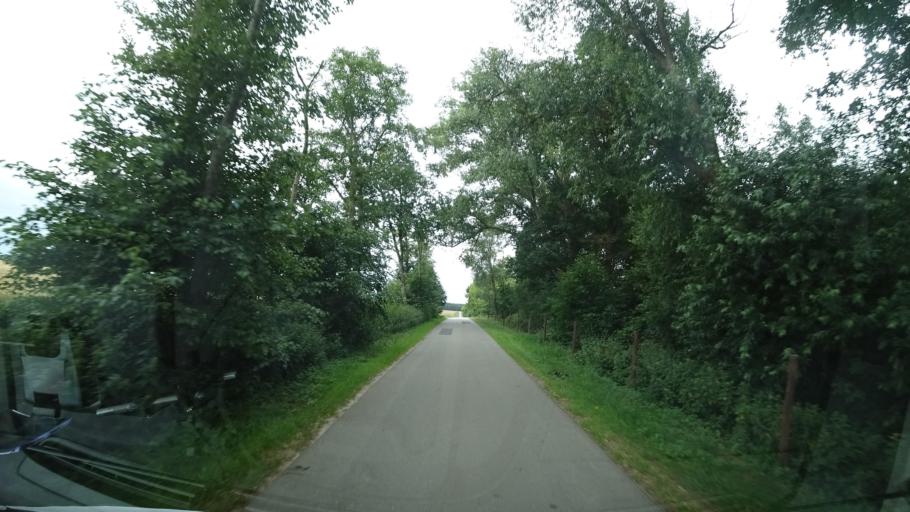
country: DE
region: Mecklenburg-Vorpommern
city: Rambin
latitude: 54.3217
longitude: 13.2023
